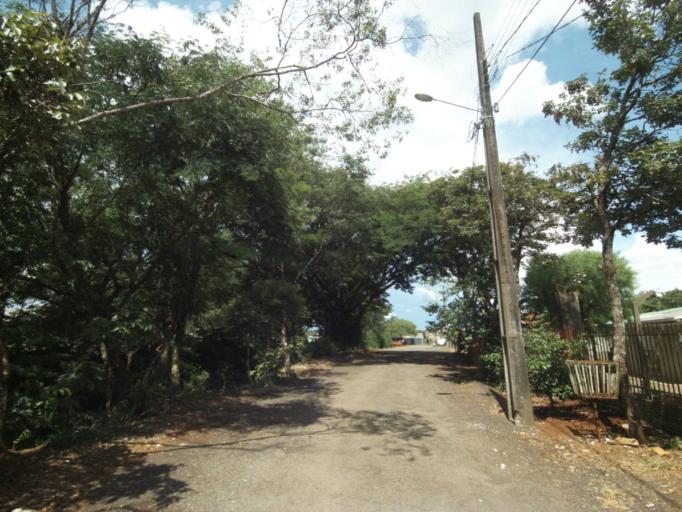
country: BR
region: Parana
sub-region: Guaraniacu
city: Guaraniacu
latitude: -25.0966
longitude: -52.8776
